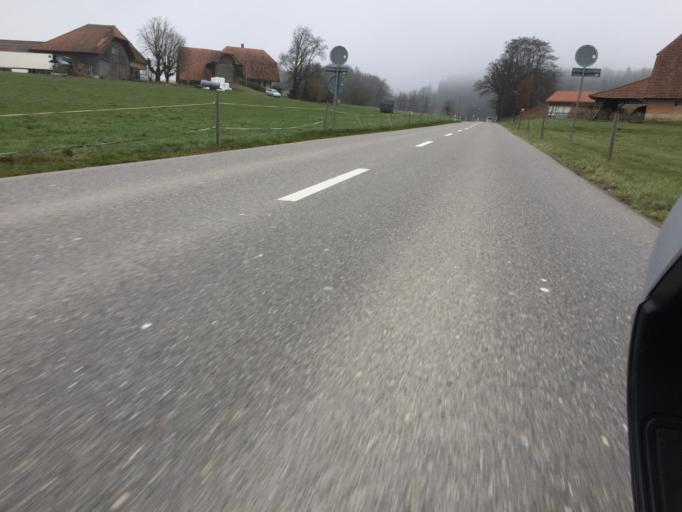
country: CH
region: Bern
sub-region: Seeland District
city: Grossaffoltern
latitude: 47.0834
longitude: 7.4042
